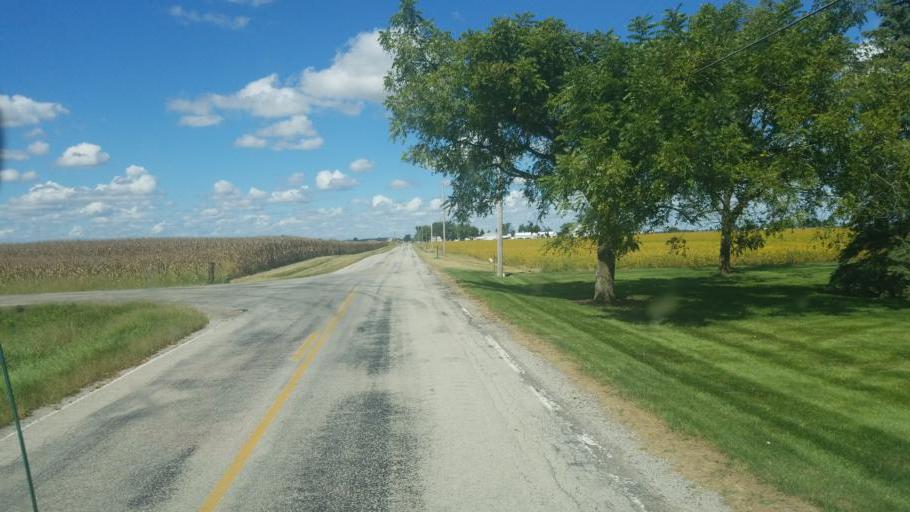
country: US
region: Ohio
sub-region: Madison County
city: West Jefferson
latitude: 40.0200
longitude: -83.3657
